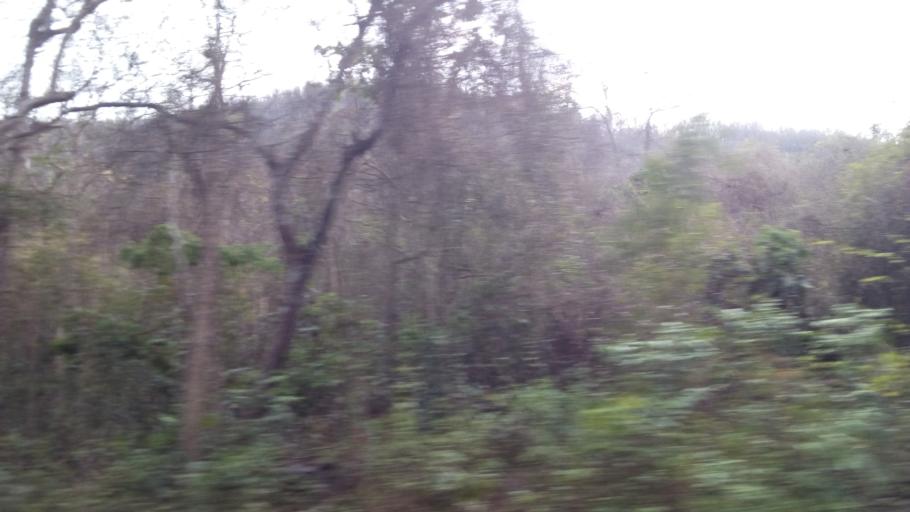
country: TH
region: Sara Buri
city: Saraburi
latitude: 14.4520
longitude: 100.9533
